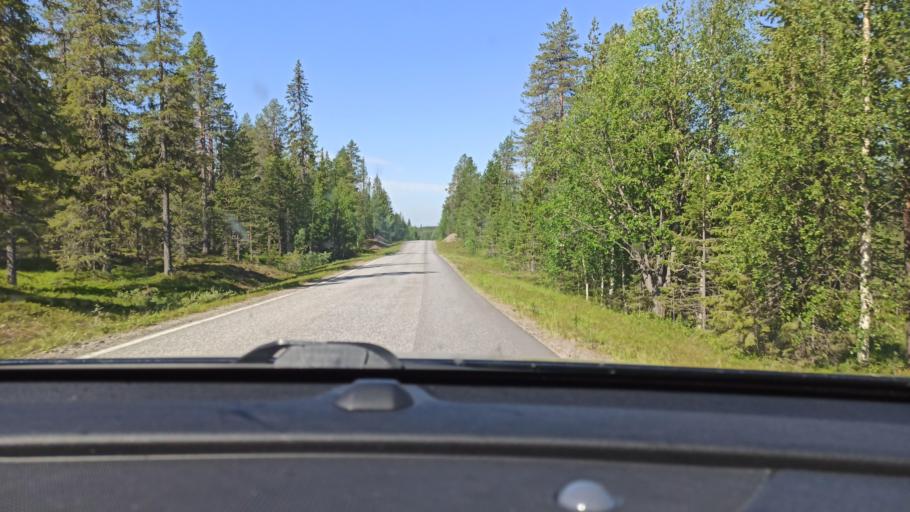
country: FI
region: Lapland
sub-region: Tunturi-Lappi
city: Kolari
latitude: 67.6827
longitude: 24.1338
